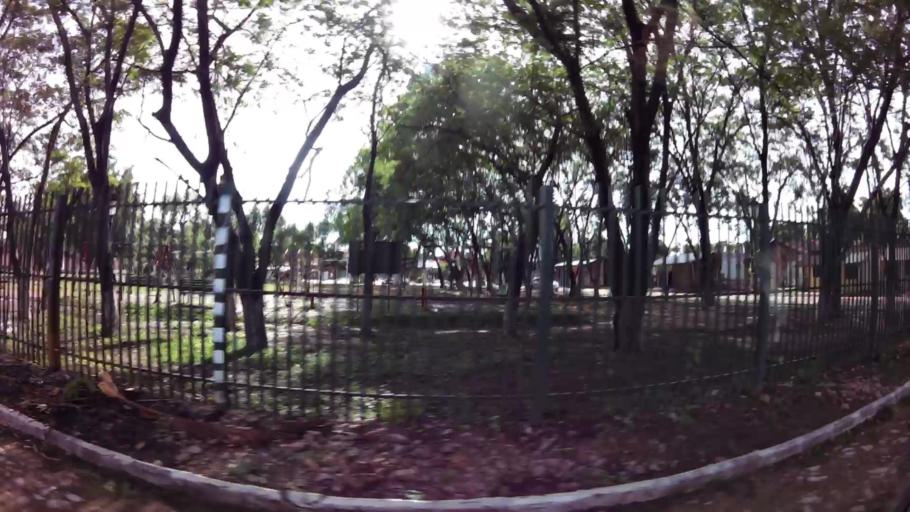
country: PY
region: Central
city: Limpio
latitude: -25.1682
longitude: -57.4798
